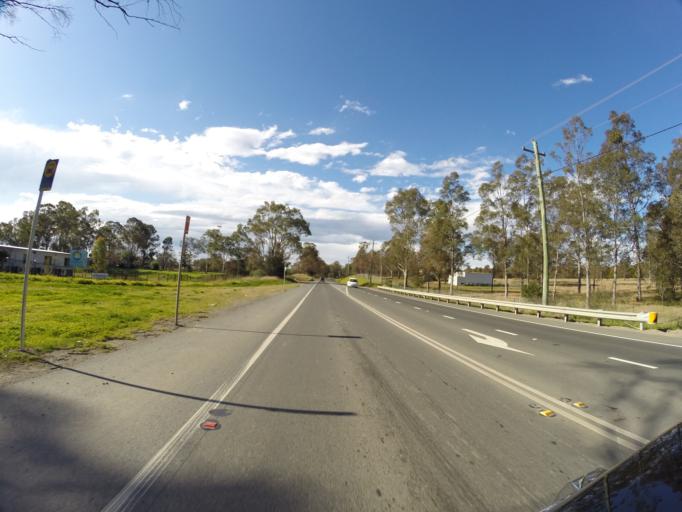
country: AU
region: New South Wales
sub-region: Fairfield
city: Cecil Park
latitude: -33.8772
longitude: 150.8263
